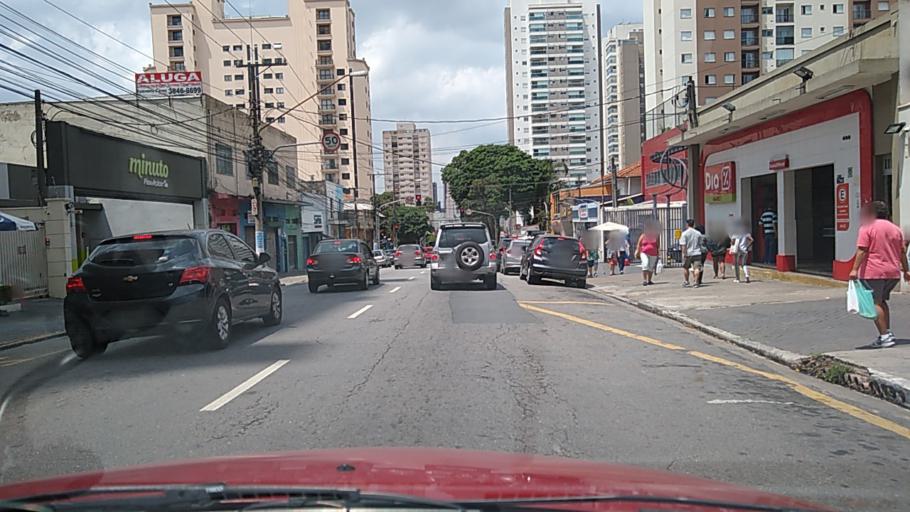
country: BR
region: Sao Paulo
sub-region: Diadema
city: Diadema
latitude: -23.6269
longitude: -46.6354
